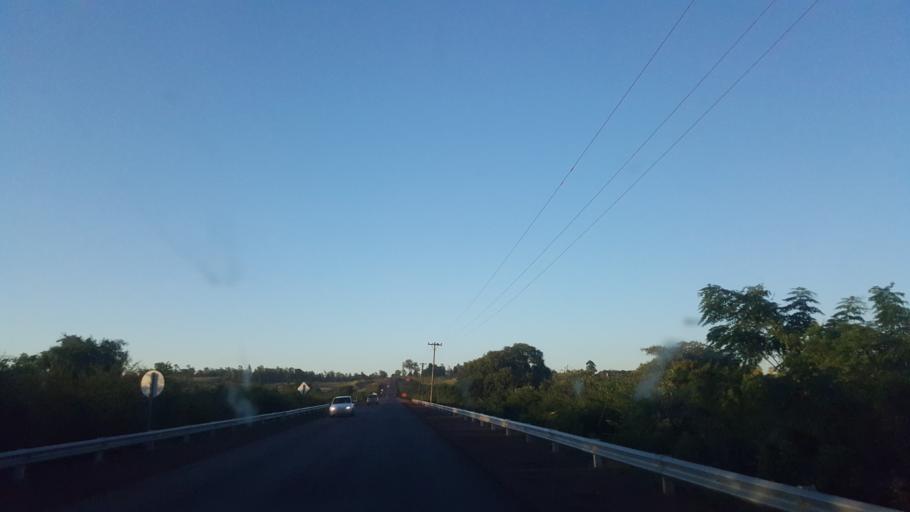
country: AR
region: Corrientes
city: Santo Tome
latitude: -28.5301
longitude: -56.0535
